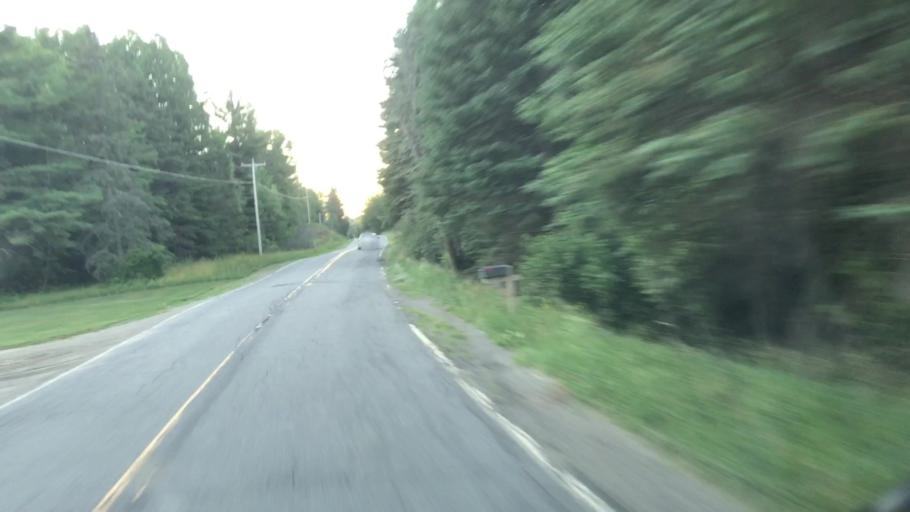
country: US
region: Maine
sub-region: Penobscot County
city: Medway
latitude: 45.6073
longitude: -68.2562
